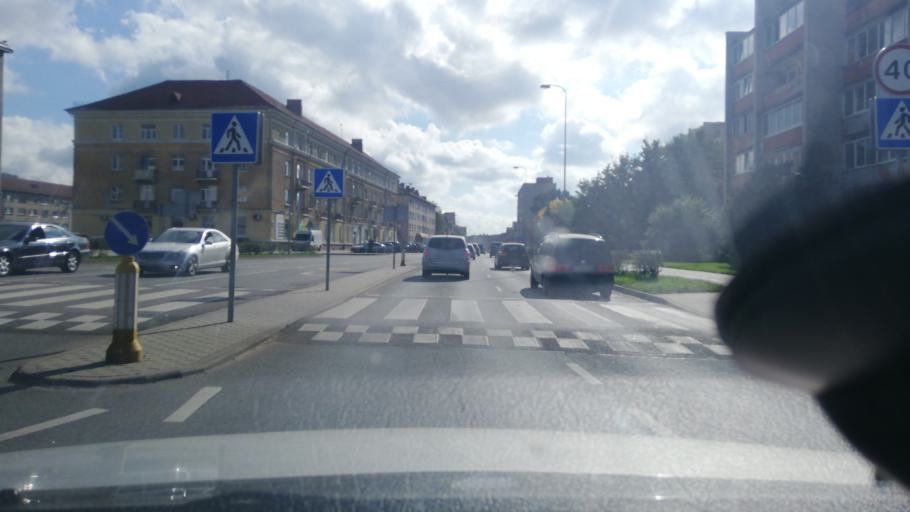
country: LT
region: Klaipedos apskritis
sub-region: Klaipeda
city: Klaipeda
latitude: 55.6825
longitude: 21.1503
